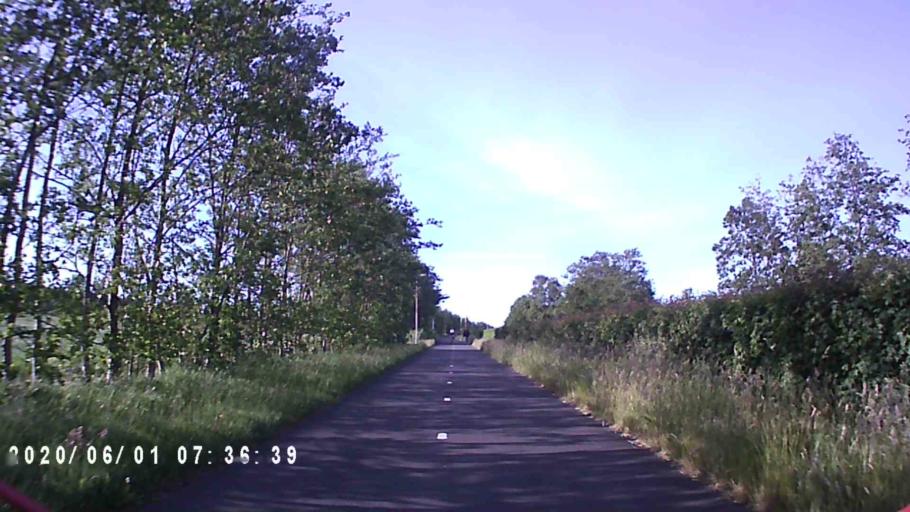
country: NL
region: Friesland
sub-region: Gemeente Dantumadiel
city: Damwald
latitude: 53.3023
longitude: 5.9952
